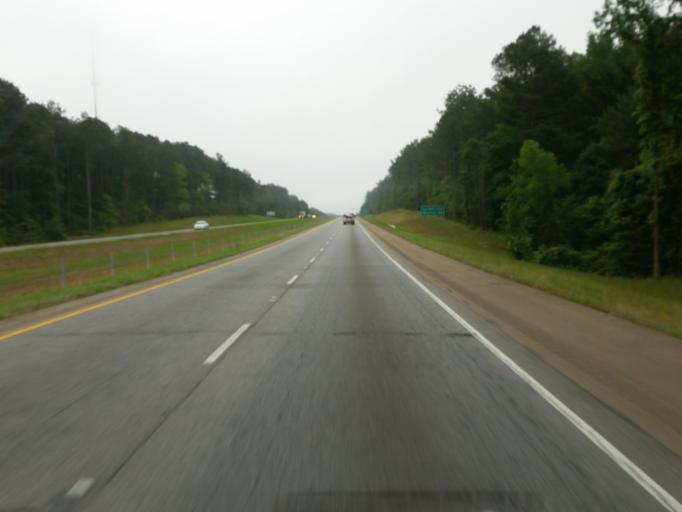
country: US
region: Louisiana
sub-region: Webster Parish
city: Minden
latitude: 32.5780
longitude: -93.2365
